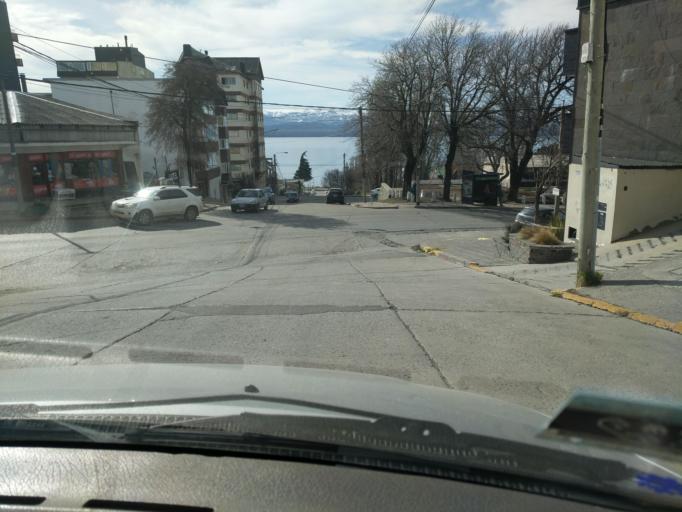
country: AR
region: Rio Negro
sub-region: Departamento de Bariloche
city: San Carlos de Bariloche
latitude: -41.1359
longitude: -71.2943
